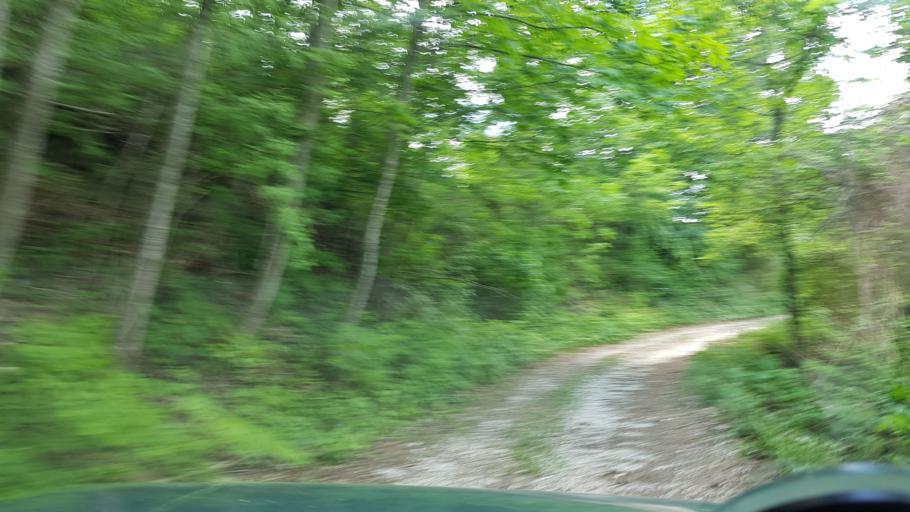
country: IT
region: Friuli Venezia Giulia
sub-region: Provincia di Udine
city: Torreano
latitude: 46.1842
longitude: 13.4248
